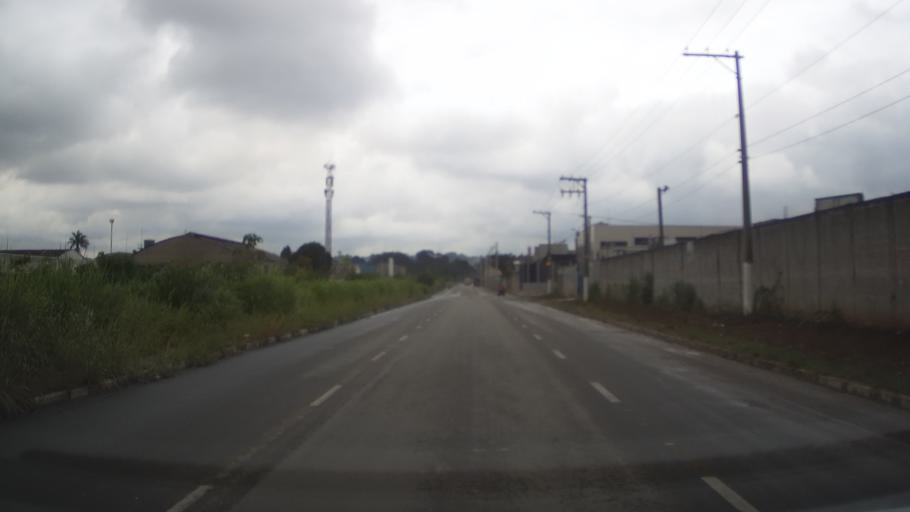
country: BR
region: Sao Paulo
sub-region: Guarulhos
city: Guarulhos
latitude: -23.4694
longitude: -46.4775
